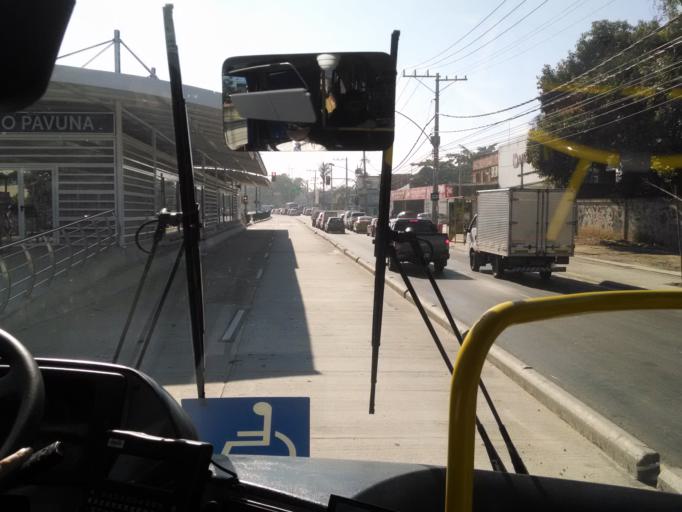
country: BR
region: Rio de Janeiro
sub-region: Sao Joao De Meriti
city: Sao Joao de Meriti
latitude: -22.9555
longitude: -43.3776
